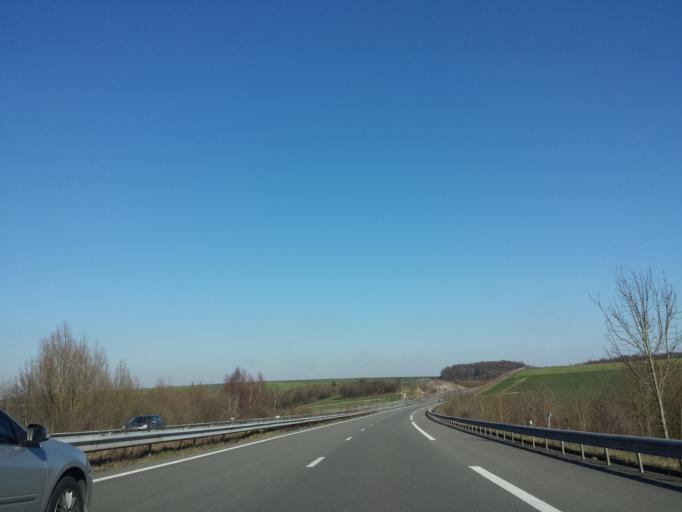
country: FR
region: Picardie
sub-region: Departement de la Somme
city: Conty
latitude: 49.6706
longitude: 2.2088
